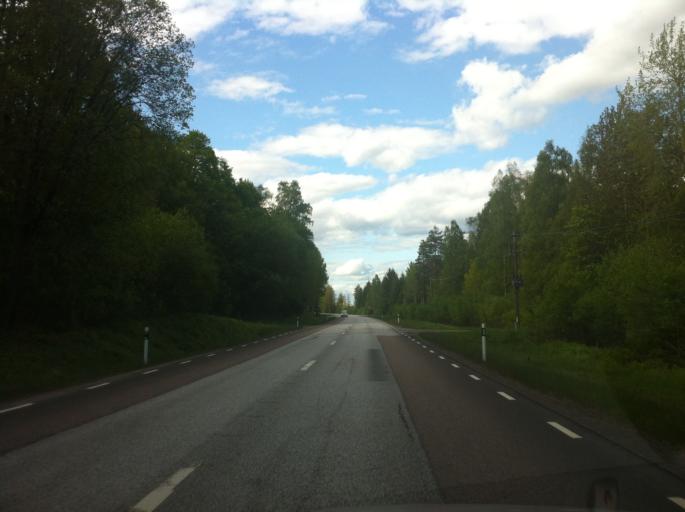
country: SE
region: Vaermland
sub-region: Storfors Kommun
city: Storfors
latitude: 59.4776
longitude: 14.2582
